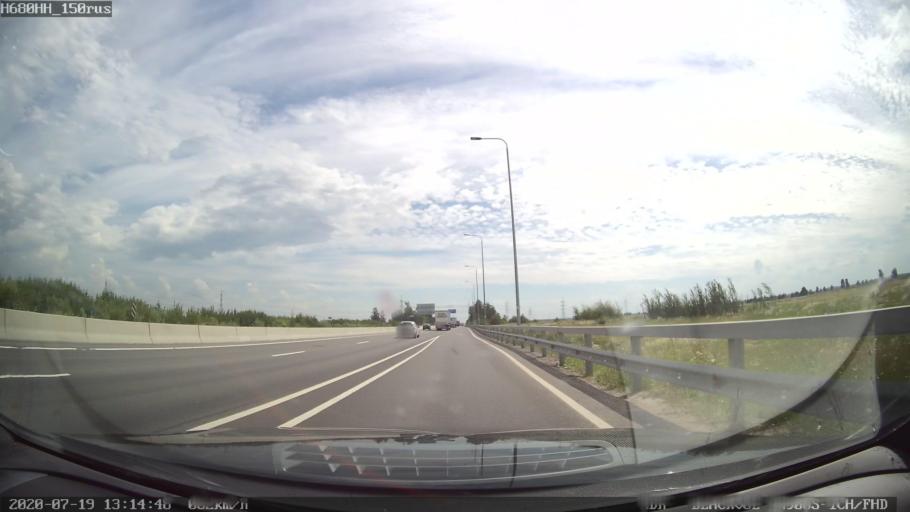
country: RU
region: St.-Petersburg
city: Kolpino
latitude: 59.7302
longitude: 30.5307
